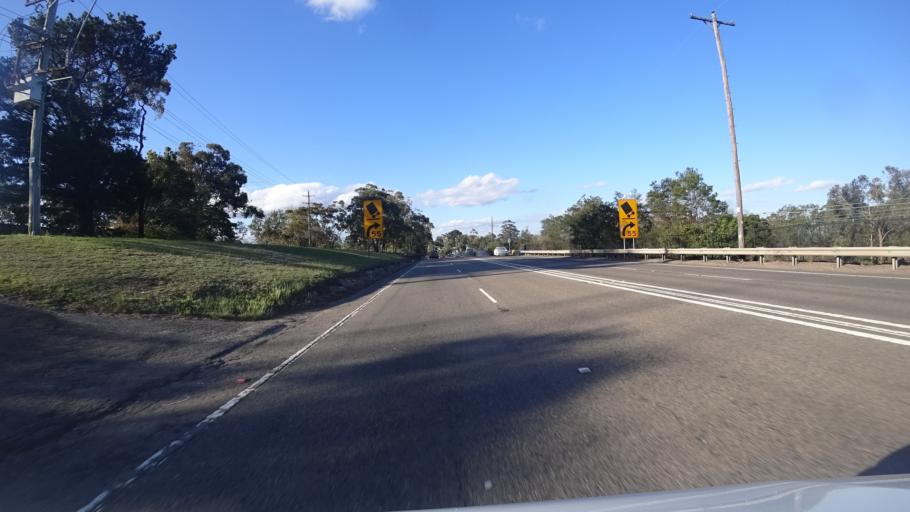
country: AU
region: New South Wales
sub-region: Blue Mountains Municipality
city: Hazelbrook
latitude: -33.7086
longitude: 150.5239
